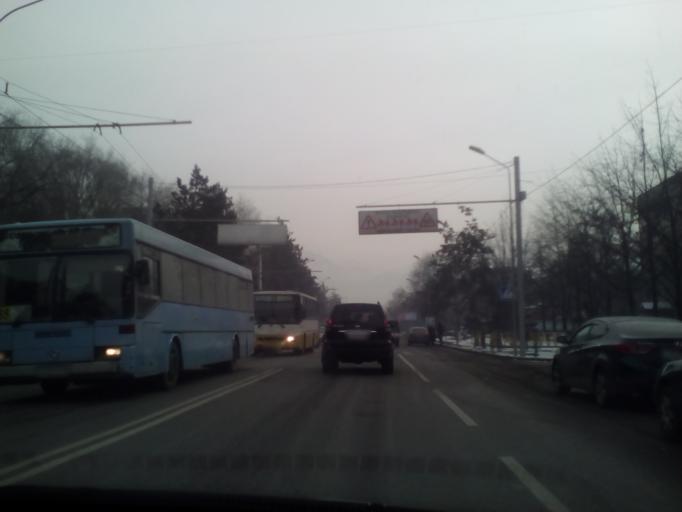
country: KZ
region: Almaty Qalasy
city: Almaty
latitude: 43.2378
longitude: 76.8300
